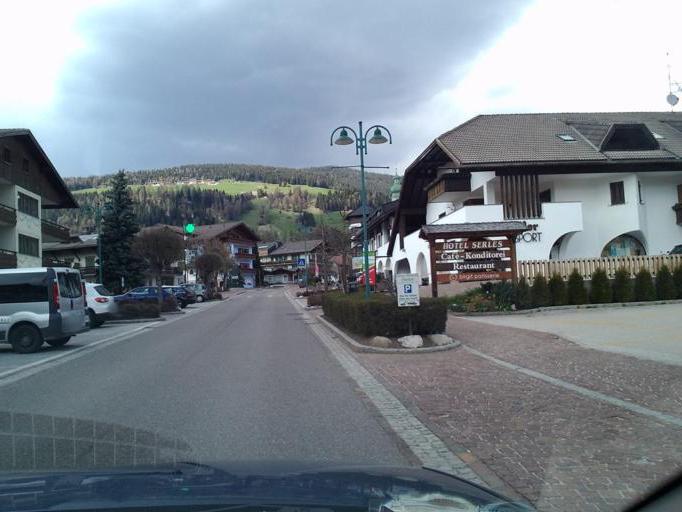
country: IT
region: Trentino-Alto Adige
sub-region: Bolzano
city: Dobbiaco
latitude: 46.7322
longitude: 12.2235
